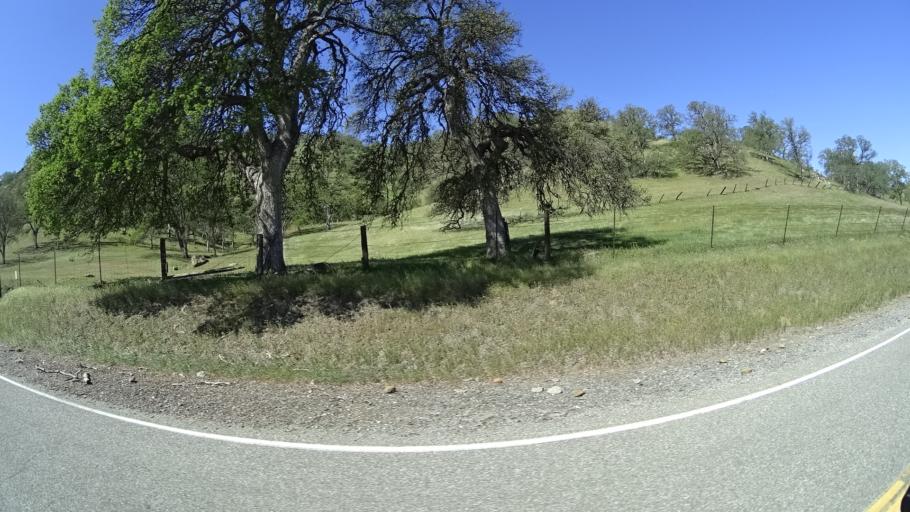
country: US
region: California
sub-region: Tehama County
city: Rancho Tehama Reserve
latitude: 39.7759
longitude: -122.5217
